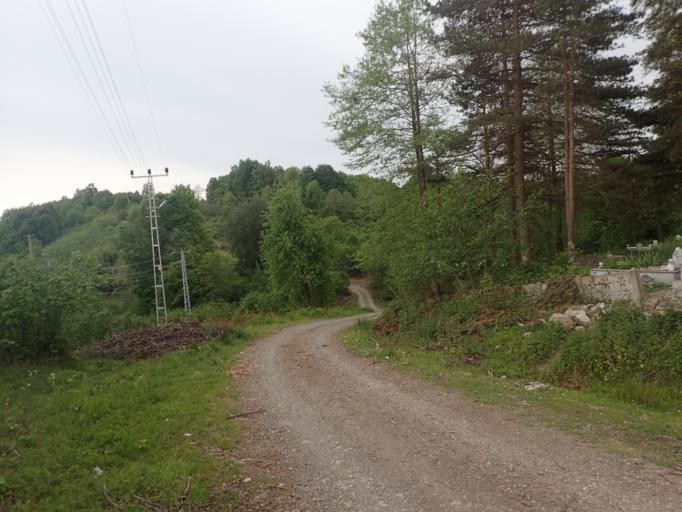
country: TR
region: Ordu
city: Akkus
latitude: 40.8823
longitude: 37.0670
